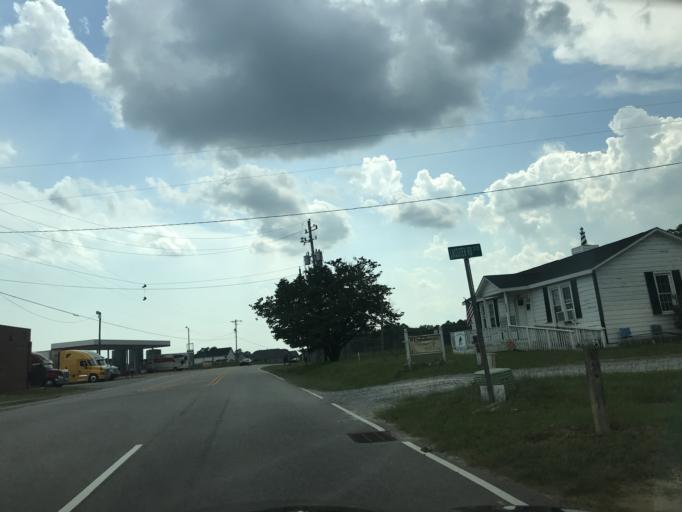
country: US
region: North Carolina
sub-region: Johnston County
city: Four Oaks
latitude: 35.5092
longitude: -78.5178
